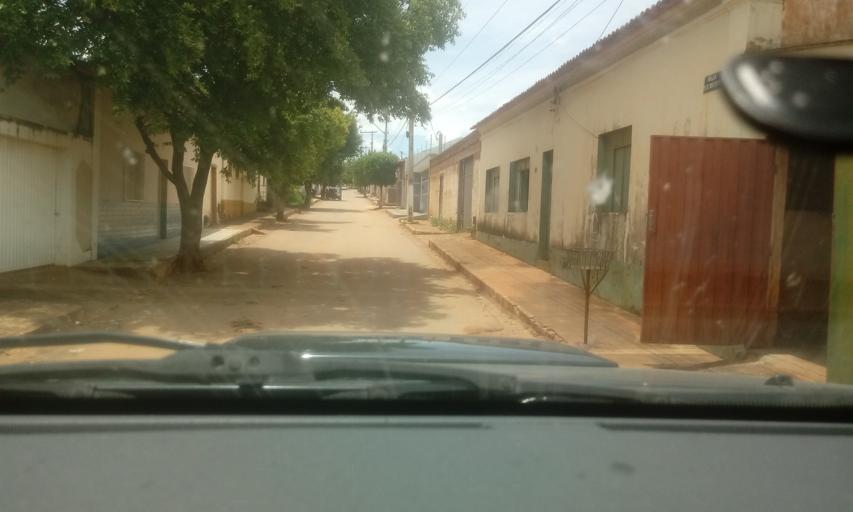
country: BR
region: Bahia
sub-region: Riacho De Santana
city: Riacho de Santana
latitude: -13.6074
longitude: -42.9439
